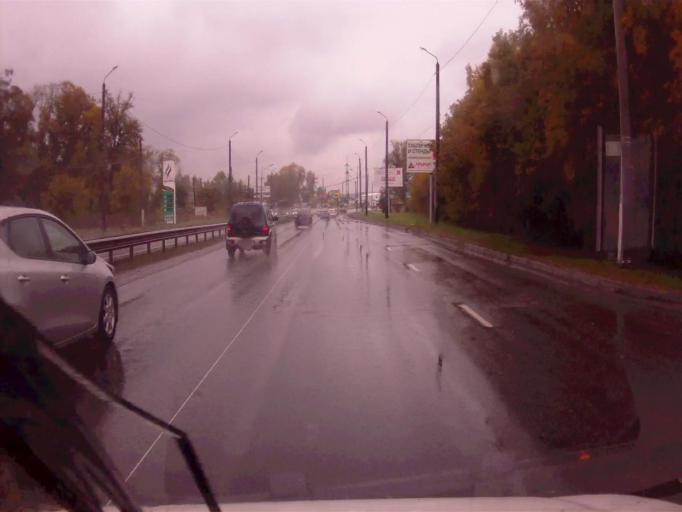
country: RU
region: Chelyabinsk
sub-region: Gorod Chelyabinsk
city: Chelyabinsk
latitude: 55.2357
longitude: 61.3644
